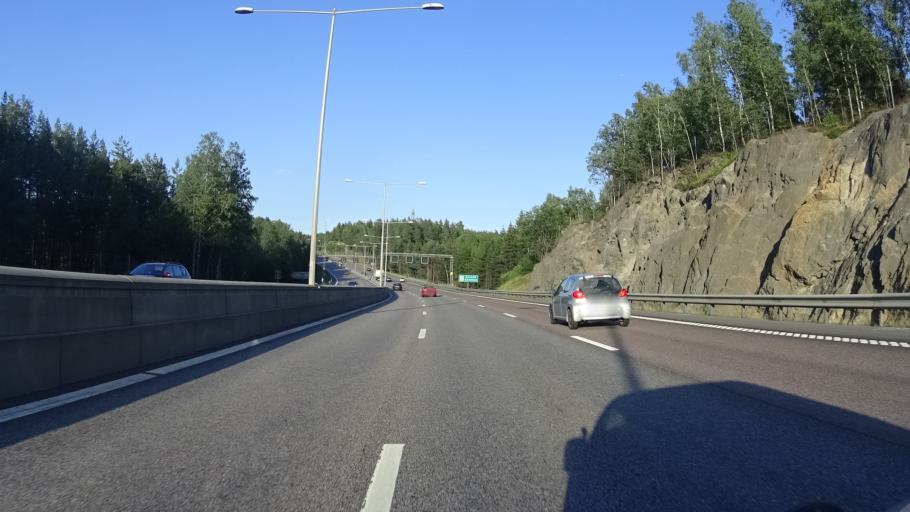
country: SE
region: Stockholm
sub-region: Salems Kommun
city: Ronninge
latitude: 59.2066
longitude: 17.6954
